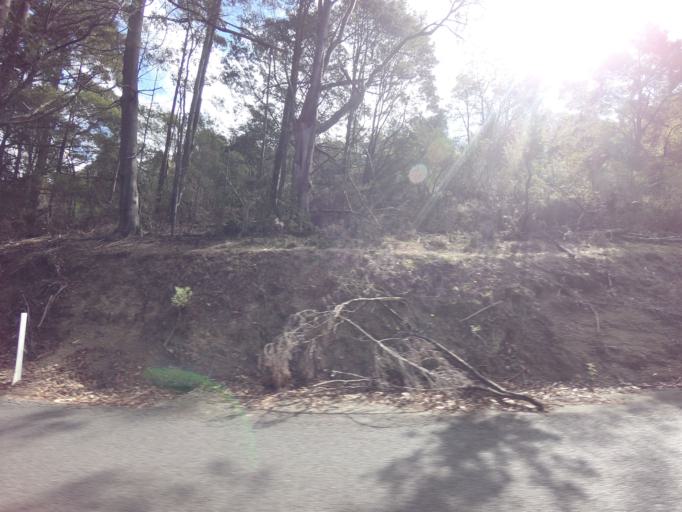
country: AU
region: Tasmania
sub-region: Break O'Day
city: St Helens
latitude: -41.6529
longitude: 148.2467
